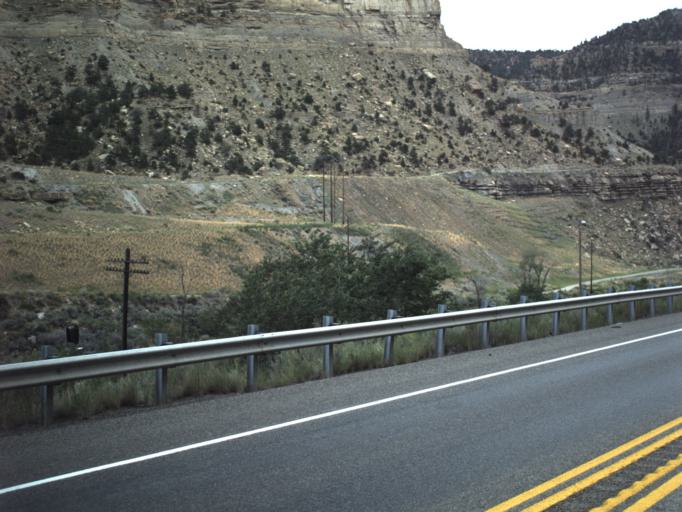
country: US
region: Utah
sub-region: Carbon County
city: Helper
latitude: 39.7145
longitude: -110.8685
